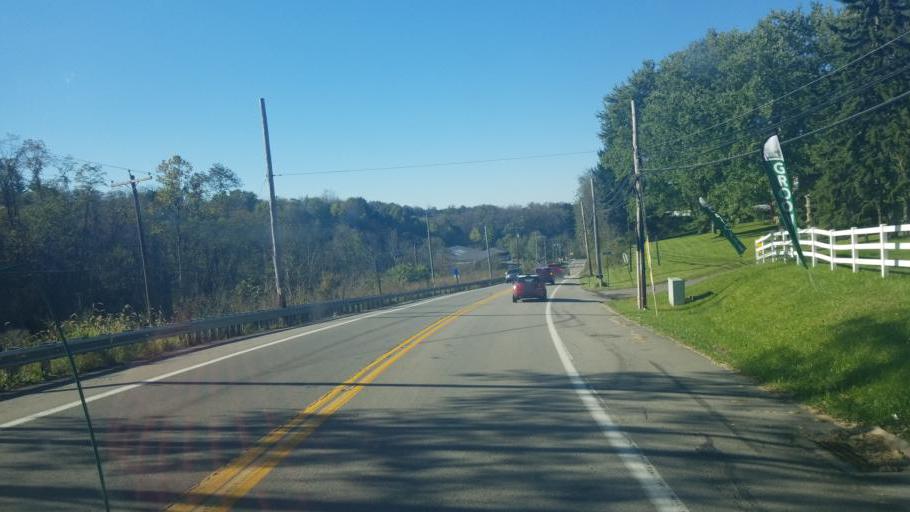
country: US
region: Pennsylvania
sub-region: Allegheny County
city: Imperial
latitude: 40.4426
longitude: -80.2408
